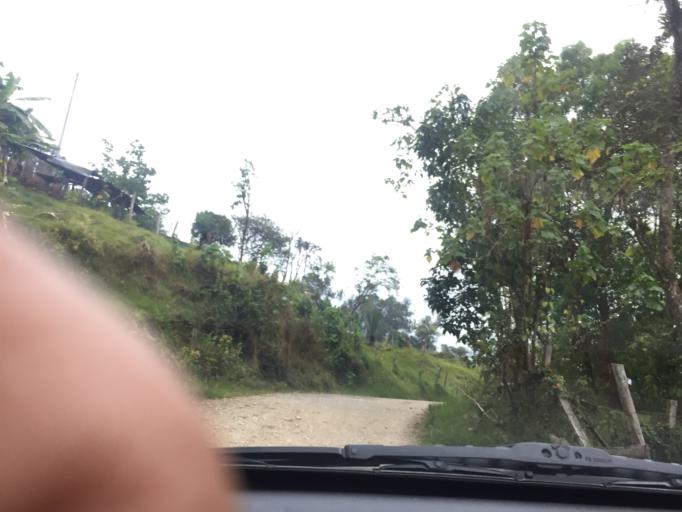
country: CO
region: Cundinamarca
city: San Antonio del Tequendama
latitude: 4.6766
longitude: -74.3744
